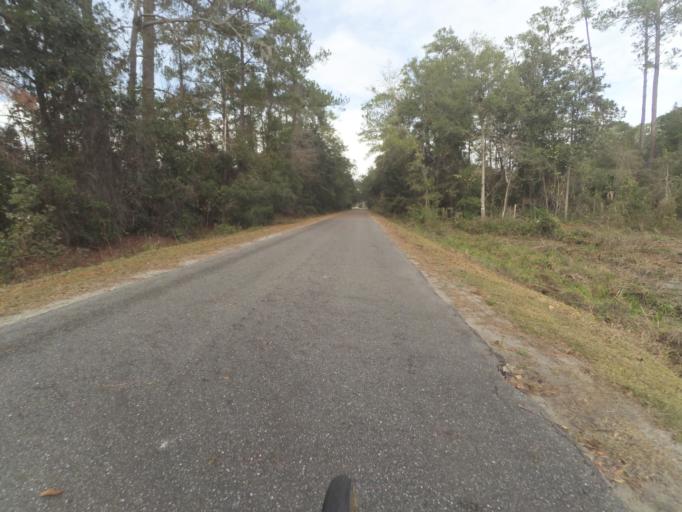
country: US
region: Florida
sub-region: Alachua County
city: Gainesville
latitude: 29.6285
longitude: -82.3115
